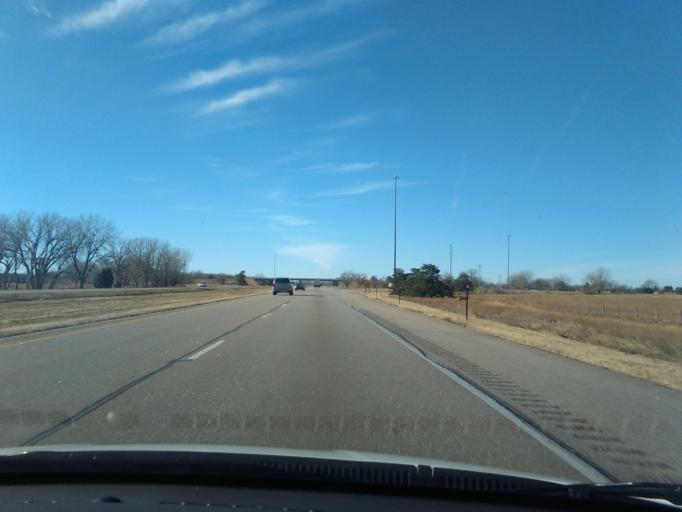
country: US
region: Nebraska
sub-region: Hall County
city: Wood River
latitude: 40.7648
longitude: -98.5819
